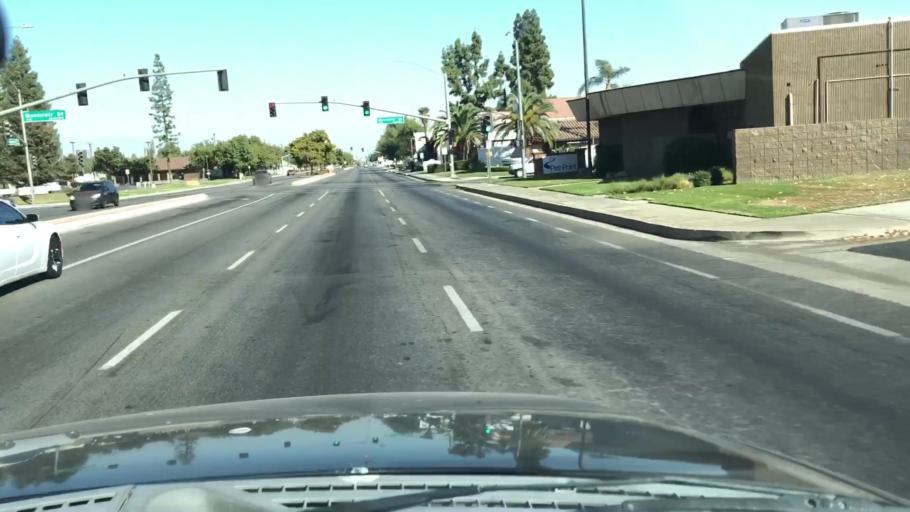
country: US
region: California
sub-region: Kern County
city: Bakersfield
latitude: 35.3542
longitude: -119.0552
